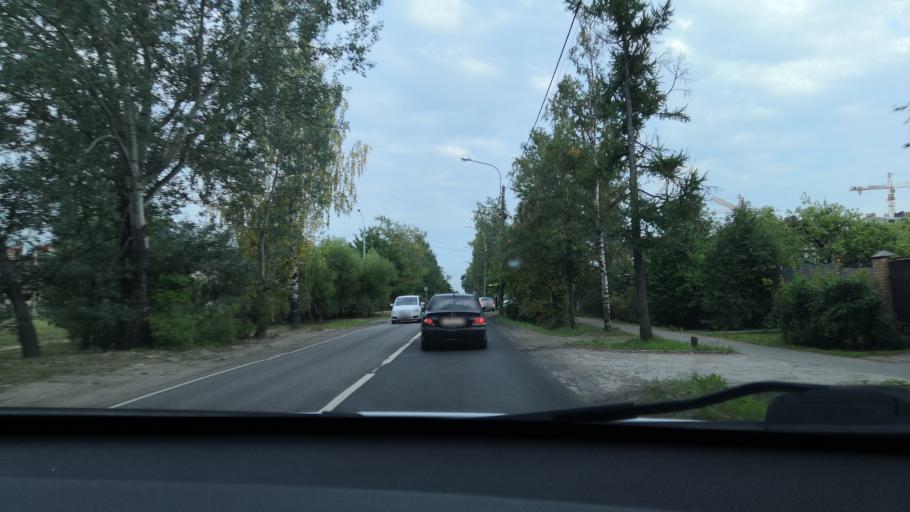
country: RU
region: St.-Petersburg
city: Pushkin
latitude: 59.6985
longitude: 30.4105
